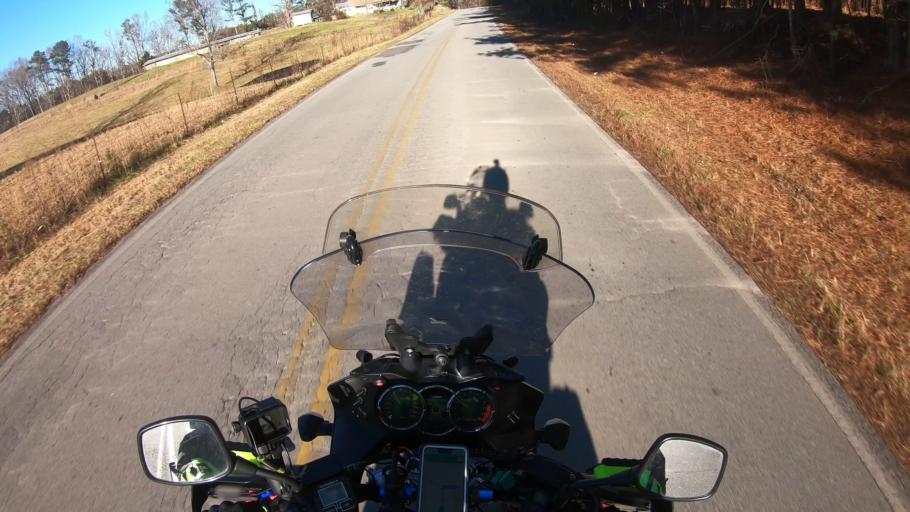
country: US
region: Georgia
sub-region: Haralson County
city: Tallapoosa
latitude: 33.8835
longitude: -85.3139
